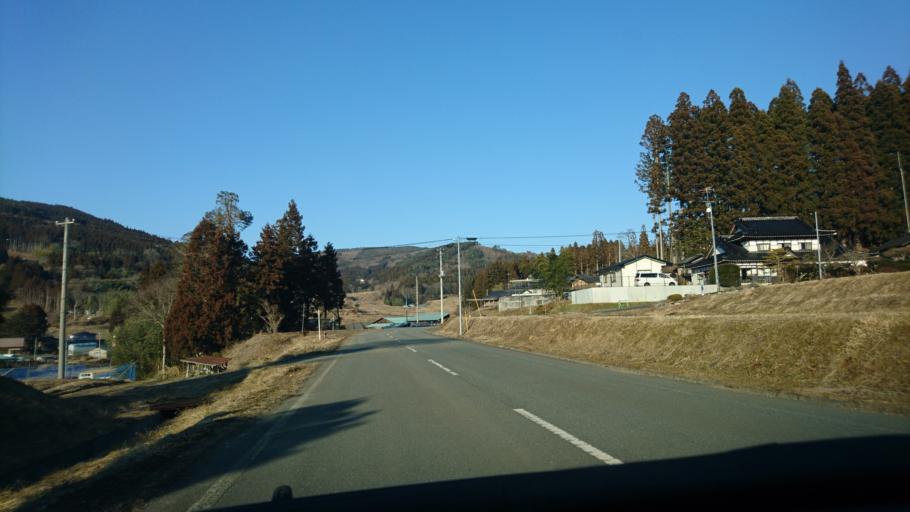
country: JP
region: Iwate
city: Ichinoseki
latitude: 38.8423
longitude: 141.3841
